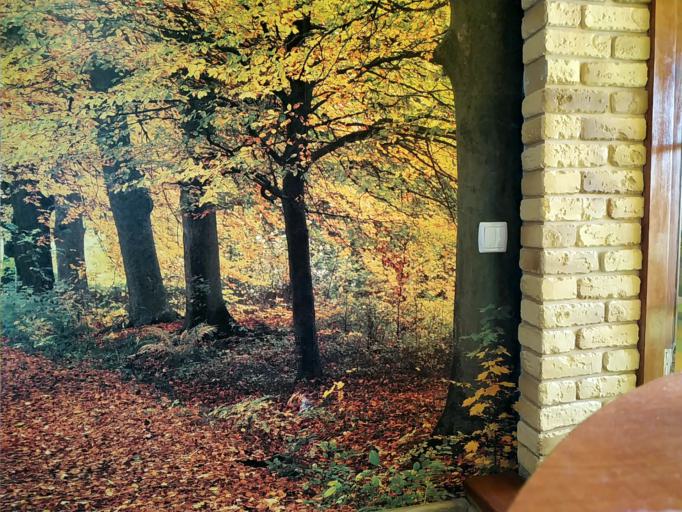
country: RU
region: Novgorod
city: Staraya Russa
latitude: 57.8416
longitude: 31.4491
